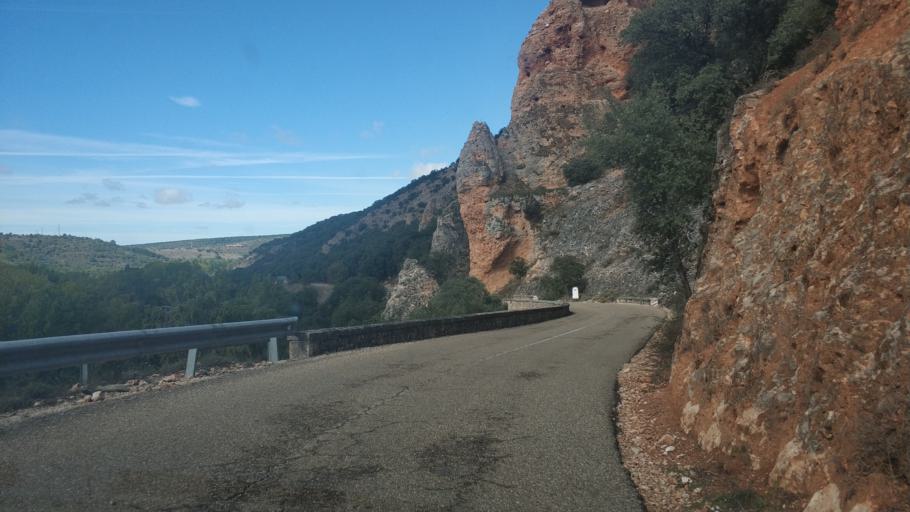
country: ES
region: Castille and Leon
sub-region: Provincia de Burgos
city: Retuerta
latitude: 42.0508
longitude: -3.4931
